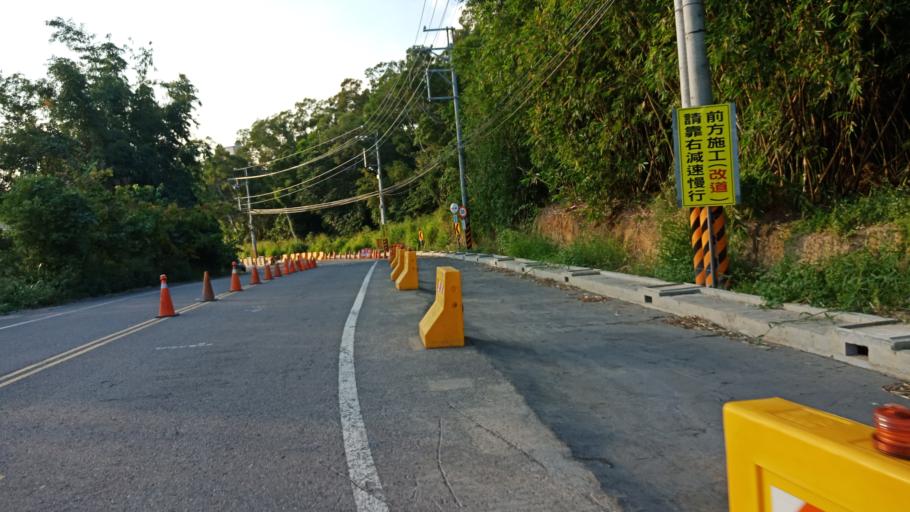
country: TW
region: Taiwan
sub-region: Hsinchu
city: Hsinchu
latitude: 24.7627
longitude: 120.9929
